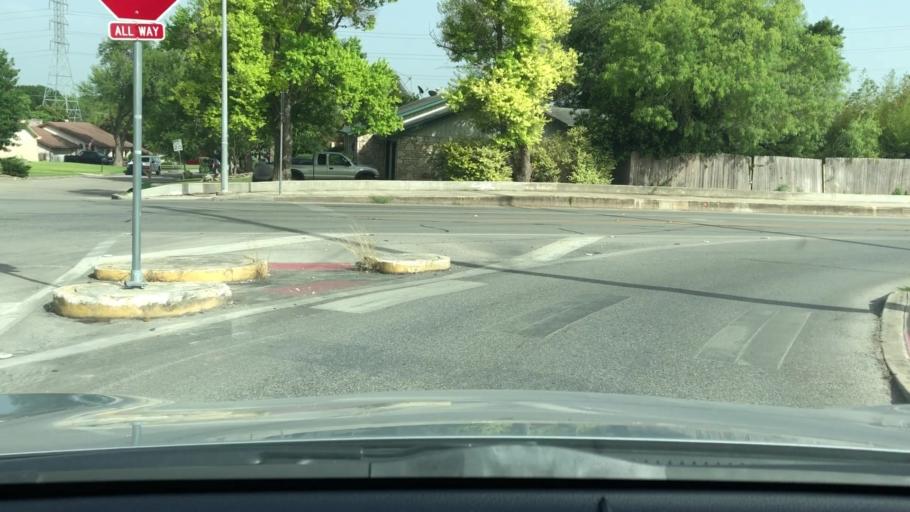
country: US
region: Texas
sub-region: Bexar County
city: Live Oak
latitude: 29.5629
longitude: -98.3245
